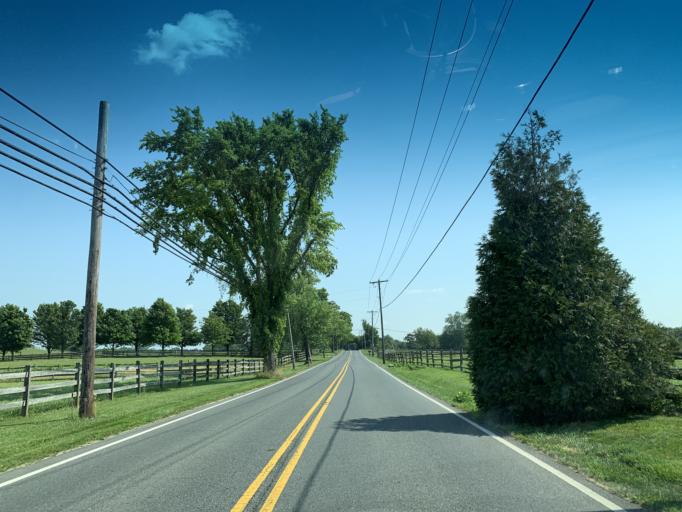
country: US
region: Maryland
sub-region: Montgomery County
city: Poolesville
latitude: 39.1608
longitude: -77.4191
